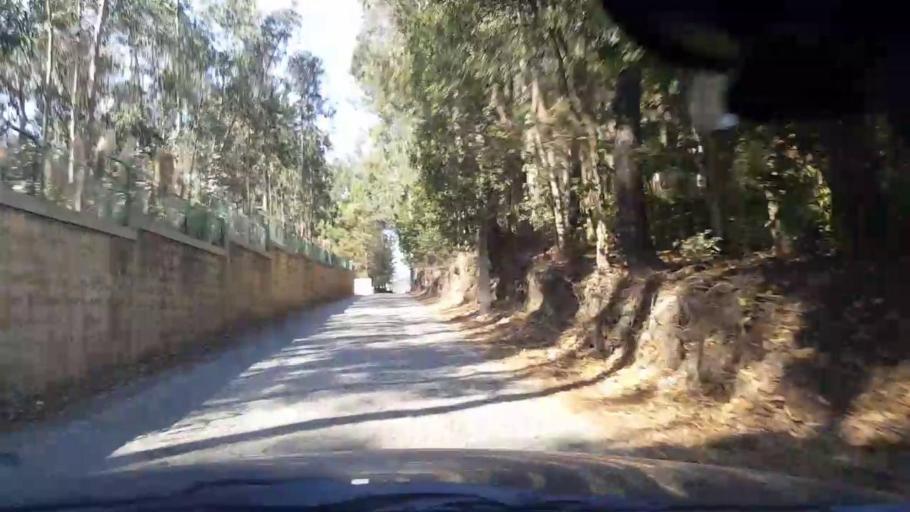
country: PT
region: Porto
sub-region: Povoa de Varzim
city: Pedroso
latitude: 41.3925
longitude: -8.7133
